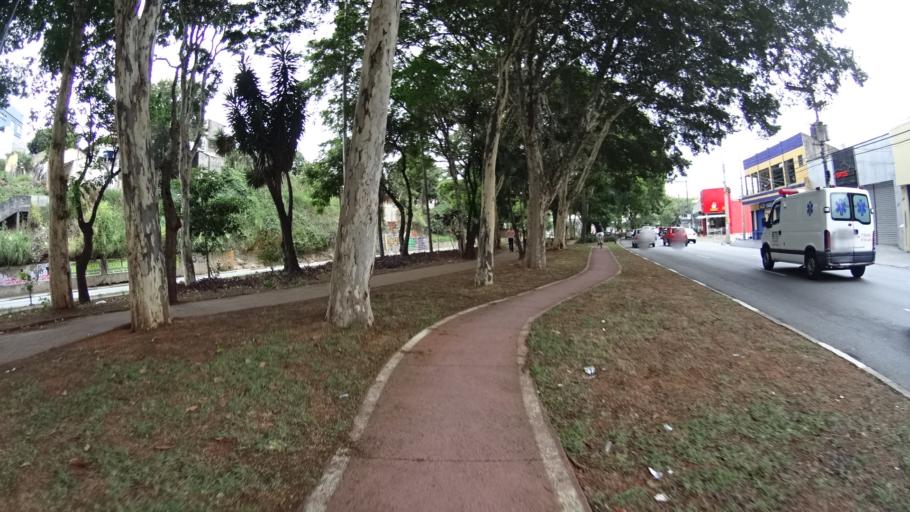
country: BR
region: Sao Paulo
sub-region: Sao Paulo
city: Sao Paulo
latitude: -23.5106
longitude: -46.6531
